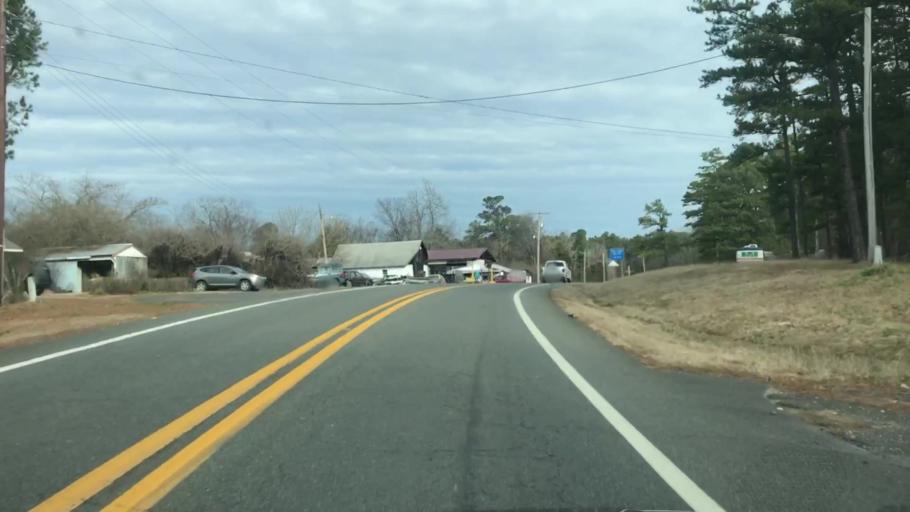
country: US
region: Arkansas
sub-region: Montgomery County
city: Mount Ida
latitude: 34.5844
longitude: -93.6632
